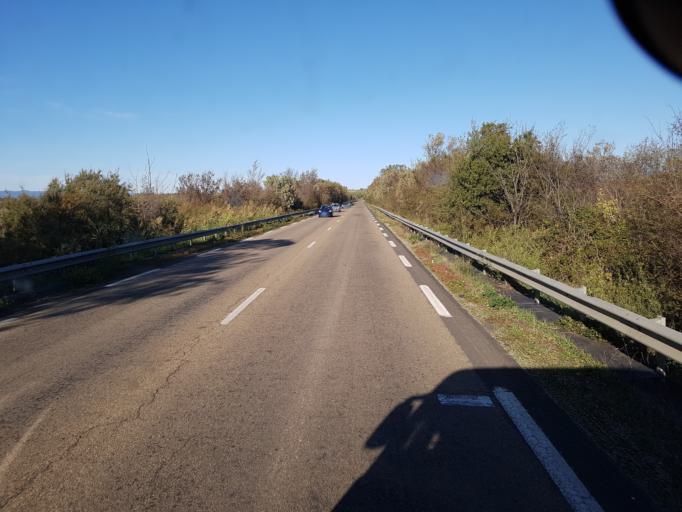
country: FR
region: Languedoc-Roussillon
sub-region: Departement de l'Aude
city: Coursan
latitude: 43.2542
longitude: 3.0719
